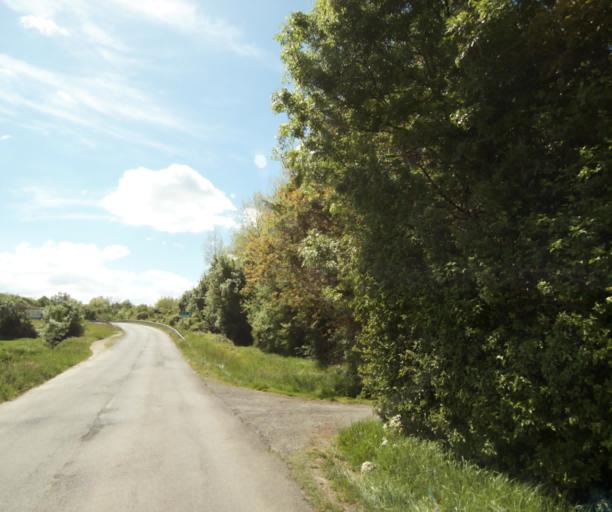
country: FR
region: Poitou-Charentes
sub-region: Departement de la Charente-Maritime
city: Chaniers
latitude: 45.7288
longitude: -0.5120
